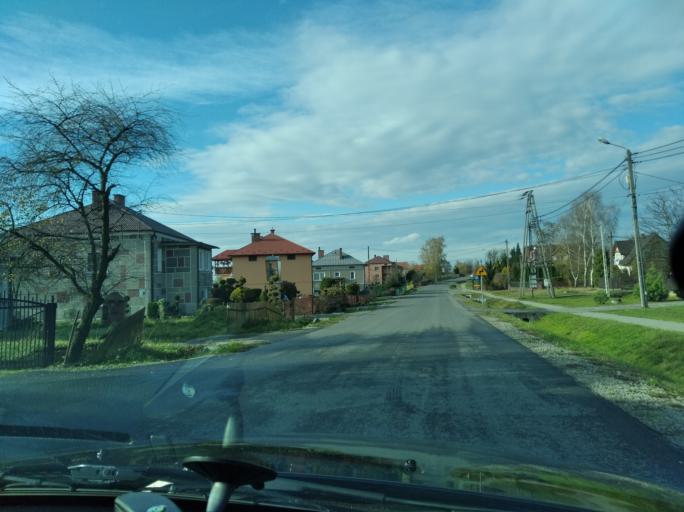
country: PL
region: Subcarpathian Voivodeship
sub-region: Powiat ropczycko-sedziszowski
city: Sedziszow Malopolski
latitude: 50.0762
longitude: 21.7468
